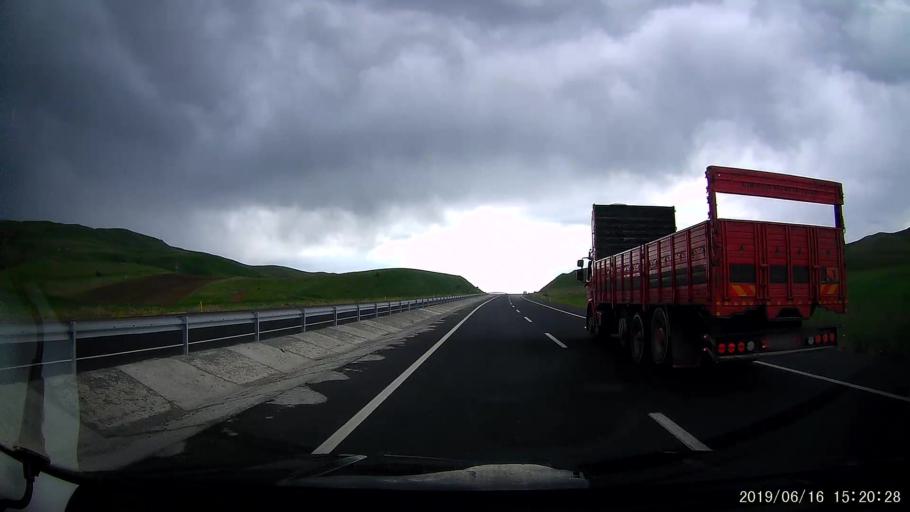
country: TR
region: Erzurum
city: Aras
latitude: 39.9747
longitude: 42.2654
